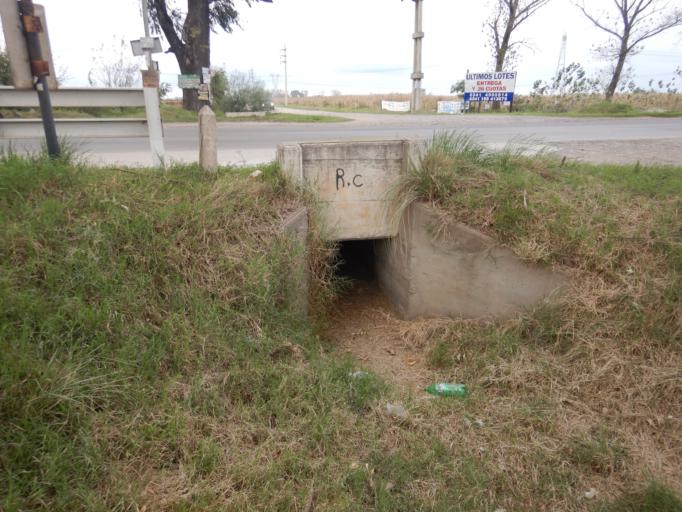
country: AR
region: Santa Fe
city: Roldan
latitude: -32.9021
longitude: -60.9276
